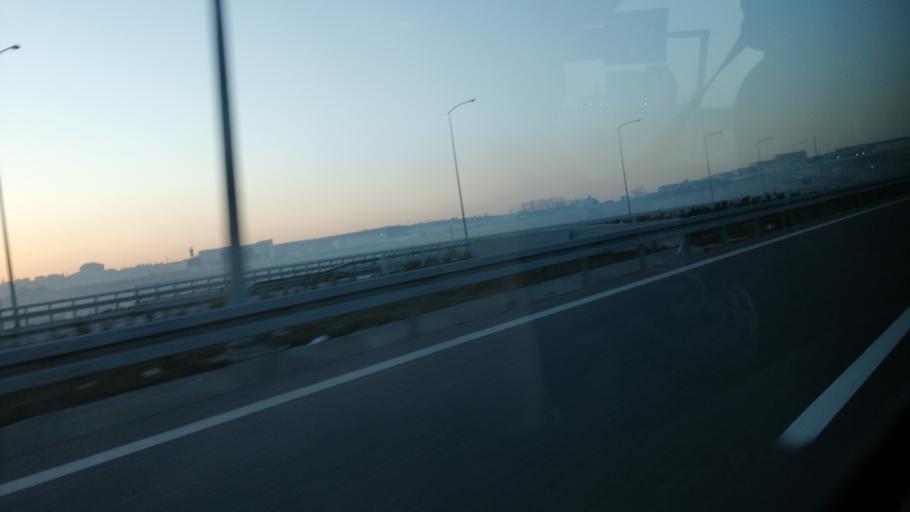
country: TR
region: Kocaeli
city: Tavsanli
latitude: 40.7947
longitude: 29.5109
